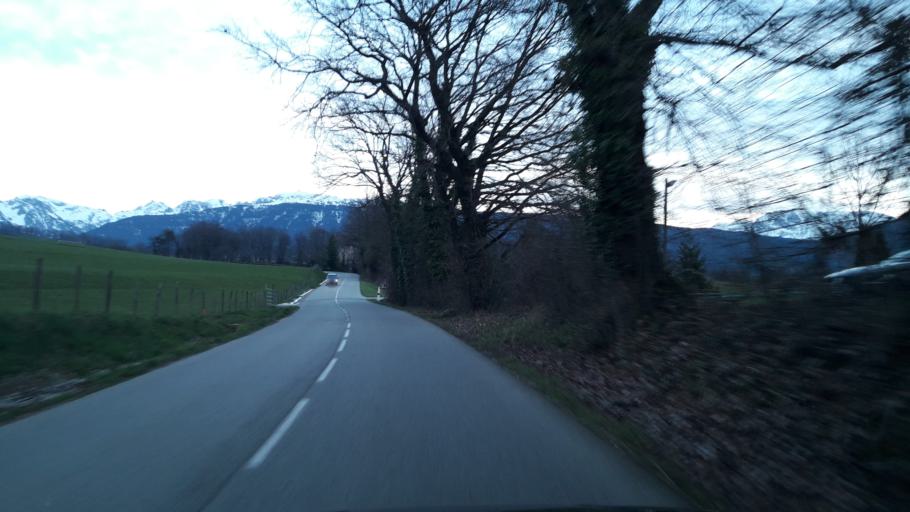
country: FR
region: Rhone-Alpes
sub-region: Departement de l'Isere
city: Herbeys
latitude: 45.1396
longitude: 5.7851
